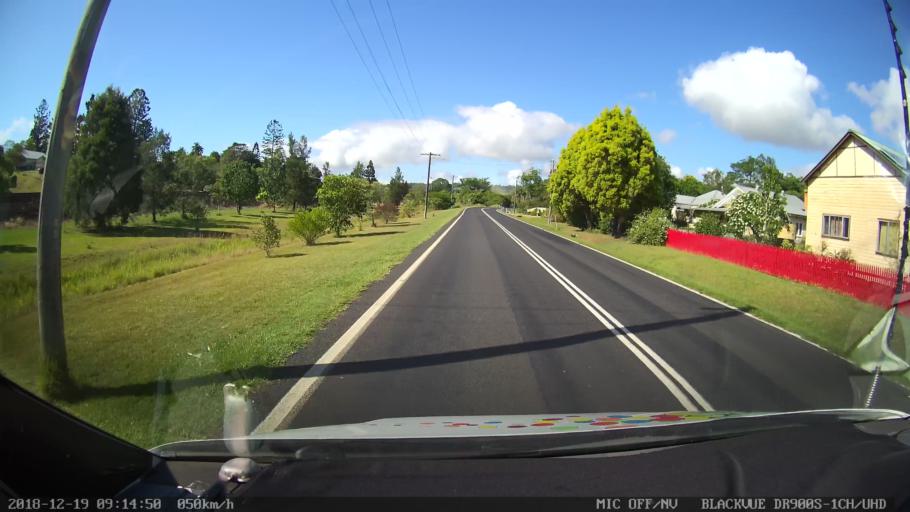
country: AU
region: New South Wales
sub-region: Kyogle
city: Kyogle
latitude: -28.5096
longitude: 152.9648
